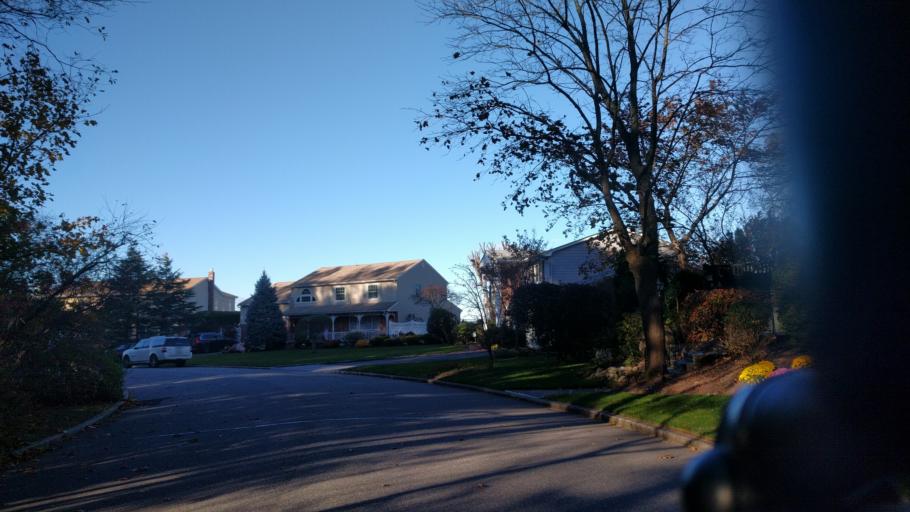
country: US
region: New York
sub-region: Nassau County
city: Bayville
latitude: 40.9118
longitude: -73.5605
